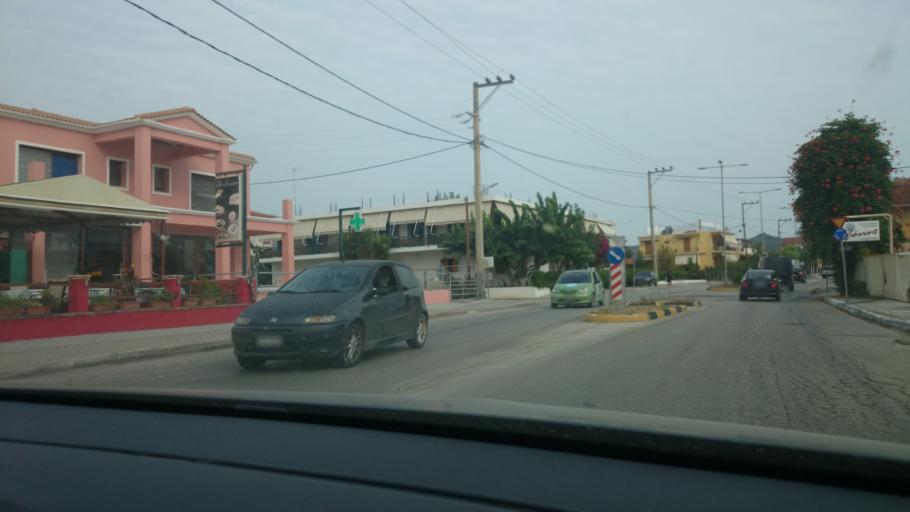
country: GR
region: Ionian Islands
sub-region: Lefkada
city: Lefkada
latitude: 38.7885
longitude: 20.7197
